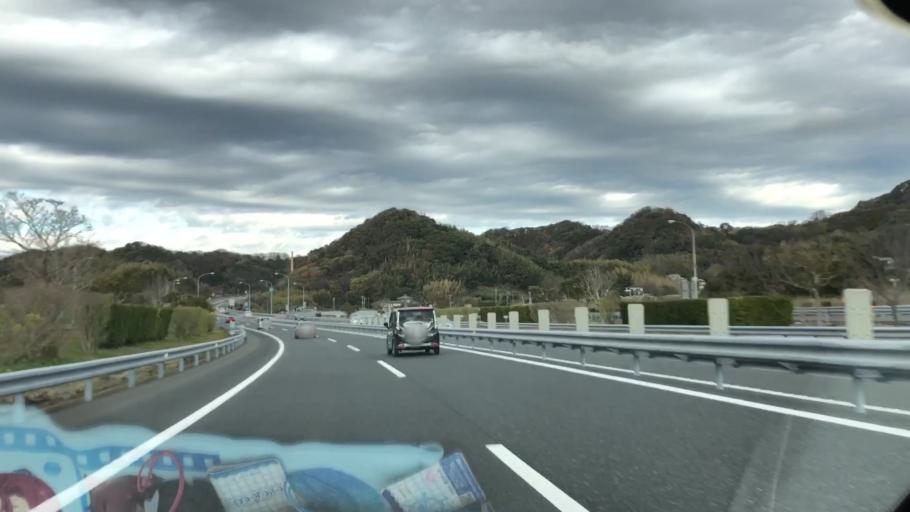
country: JP
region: Chiba
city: Tateyama
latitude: 35.0990
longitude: 139.8586
